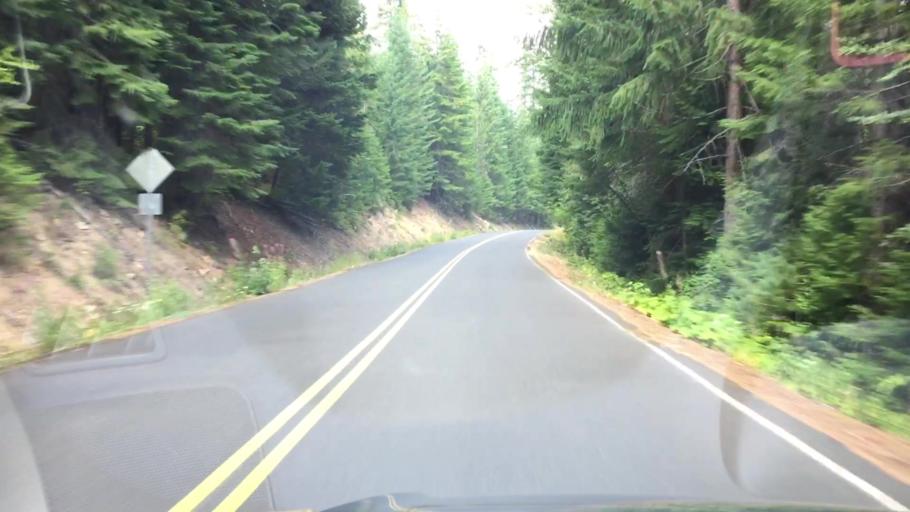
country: US
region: Washington
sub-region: Klickitat County
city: White Salmon
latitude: 46.0585
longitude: -121.5683
